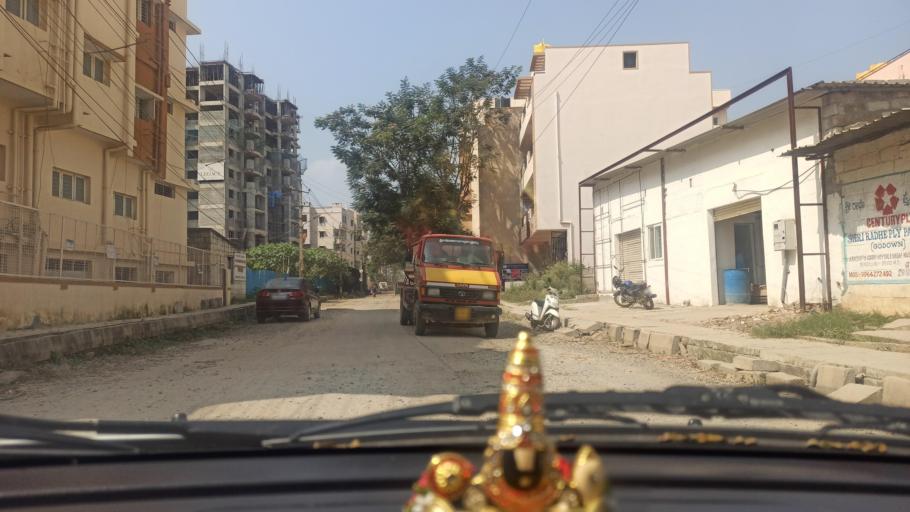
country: IN
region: Karnataka
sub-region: Bangalore Urban
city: Bangalore
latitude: 13.0237
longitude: 77.6630
